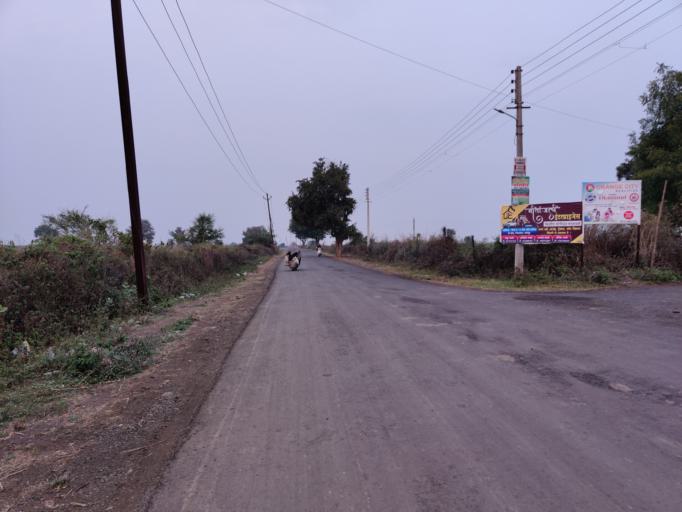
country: IN
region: Maharashtra
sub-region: Nagpur Division
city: Kamthi
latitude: 21.1967
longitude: 79.1544
